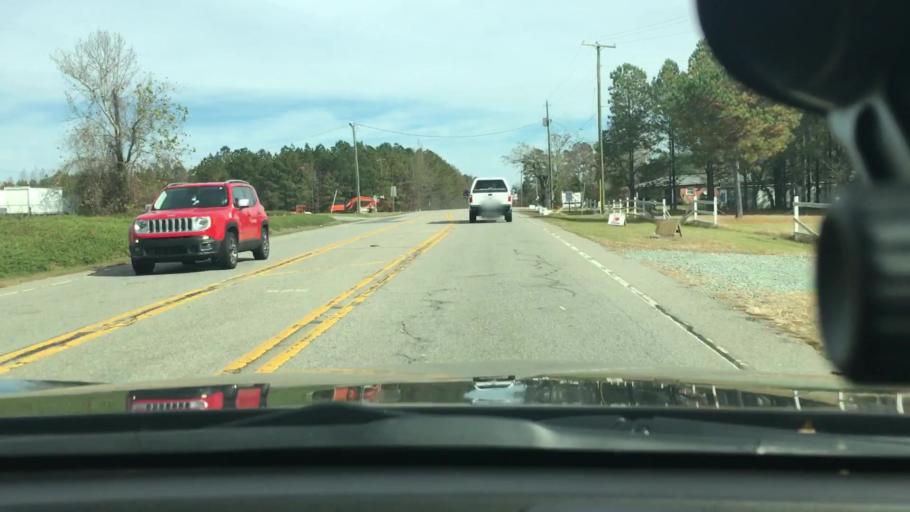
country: US
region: North Carolina
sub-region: Moore County
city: Carthage
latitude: 35.3774
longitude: -79.2902
